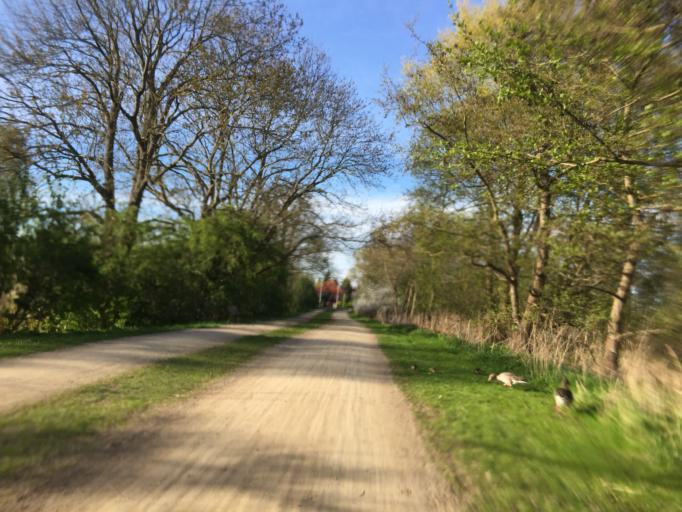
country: DK
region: Capital Region
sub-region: Gladsaxe Municipality
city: Buddinge
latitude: 55.7215
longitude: 12.5147
